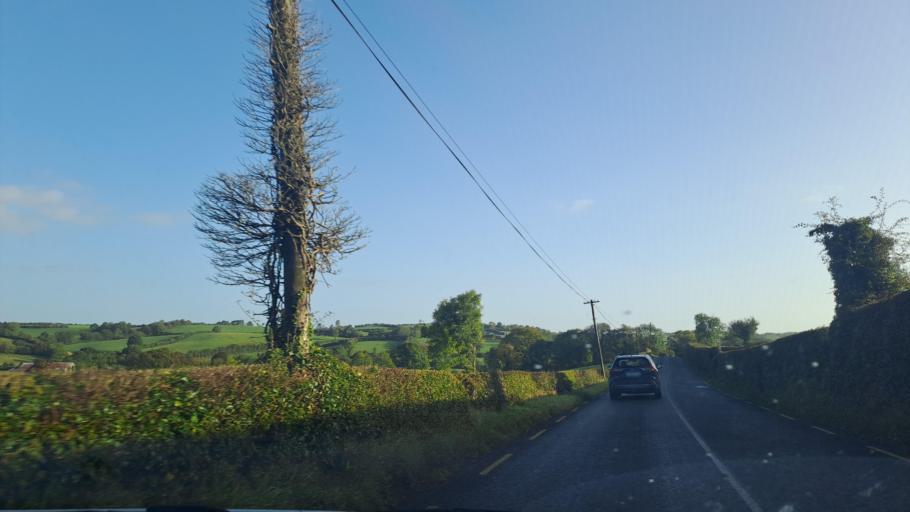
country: IE
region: Ulster
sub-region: An Cabhan
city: Kingscourt
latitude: 54.0435
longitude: -6.8695
